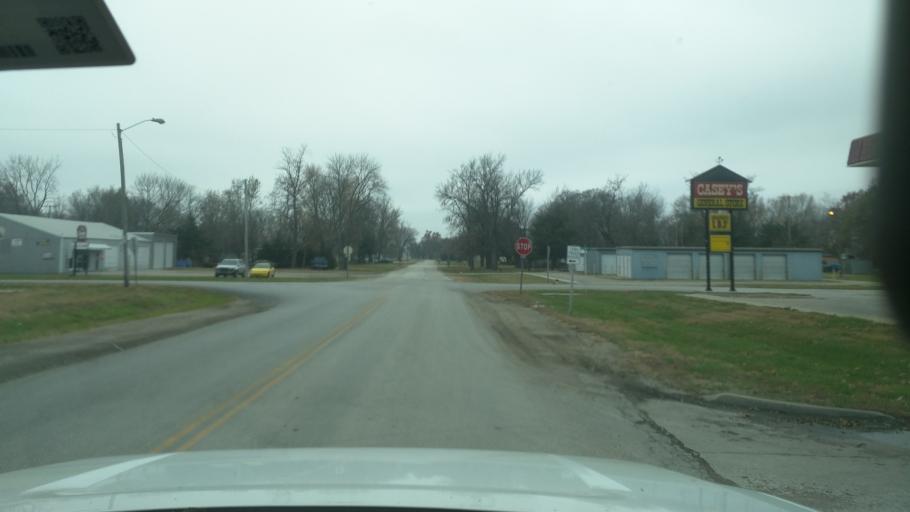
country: US
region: Kansas
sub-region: Lyon County
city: Emporia
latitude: 38.5043
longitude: -96.2623
